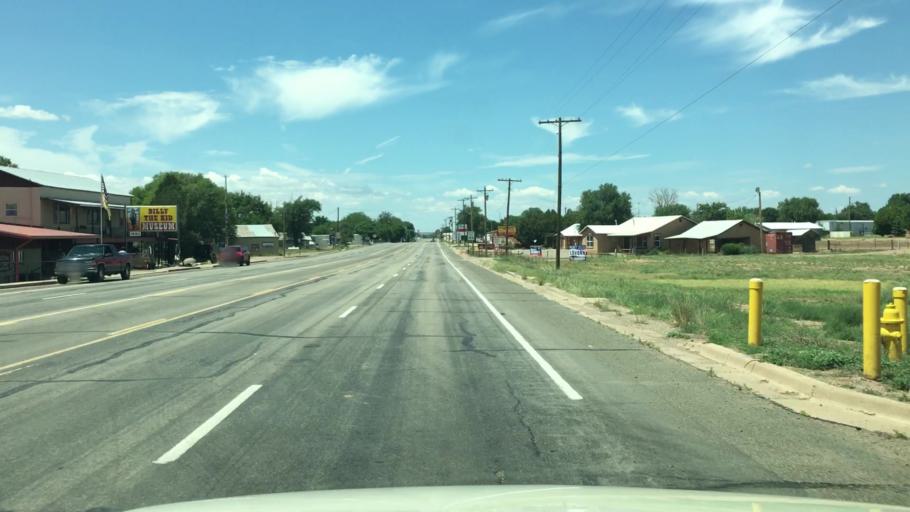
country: US
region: New Mexico
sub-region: De Baca County
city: Fort Sumner
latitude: 34.4664
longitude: -104.2287
